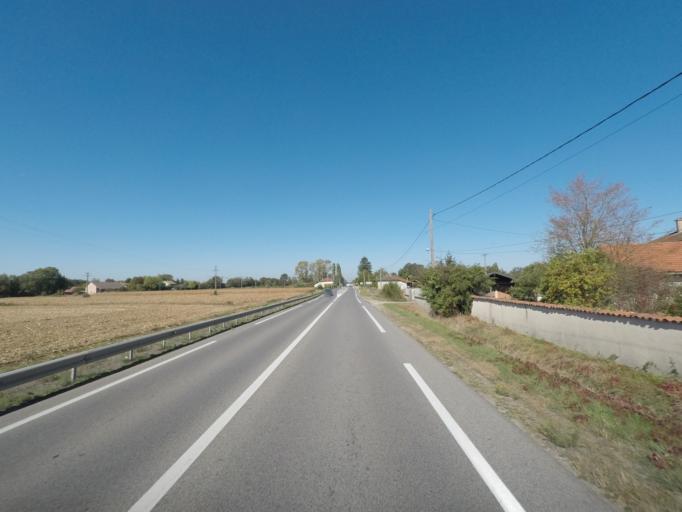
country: FR
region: Rhone-Alpes
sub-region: Departement de l'Ain
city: Viriat
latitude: 46.2463
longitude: 5.1881
